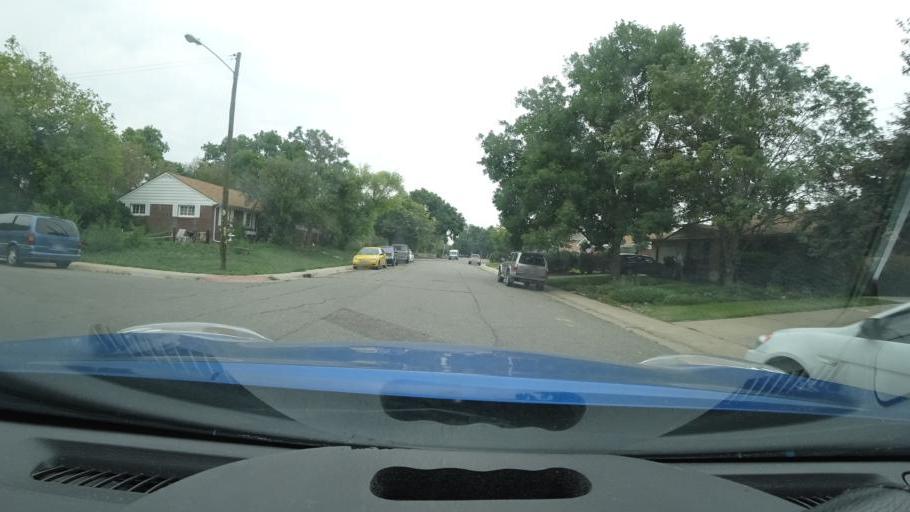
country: US
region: Colorado
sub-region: Arapahoe County
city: Glendale
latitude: 39.6865
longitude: -104.9183
